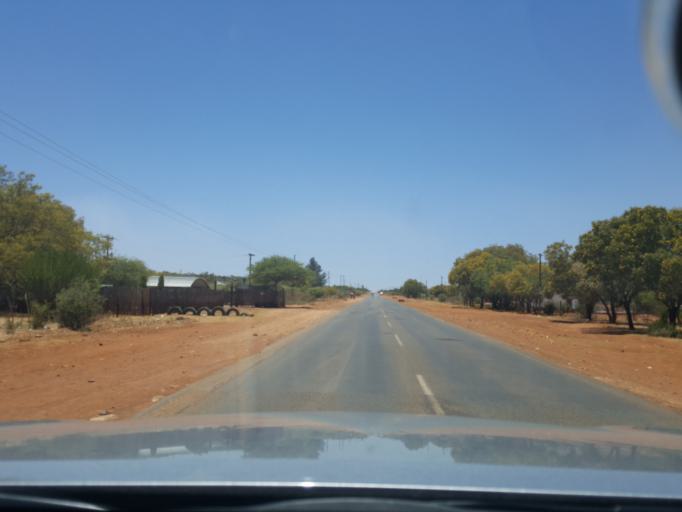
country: ZA
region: North-West
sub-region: Ngaka Modiri Molema District Municipality
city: Zeerust
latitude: -25.4485
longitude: 25.9665
